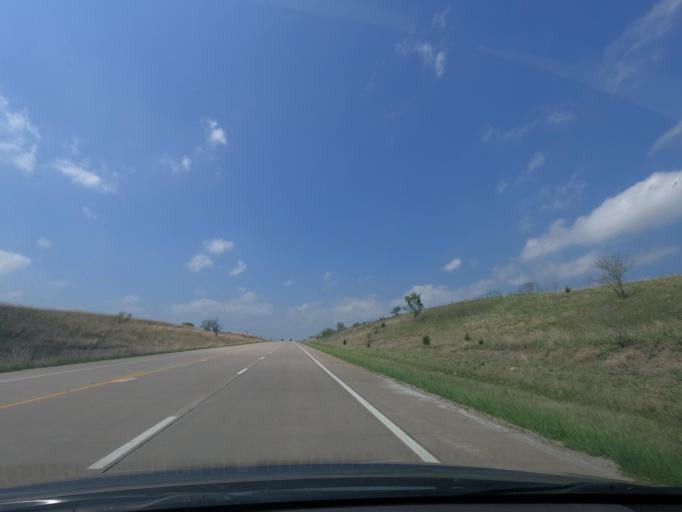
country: US
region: Kansas
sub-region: Wilson County
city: Fredonia
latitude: 37.5911
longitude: -95.8771
